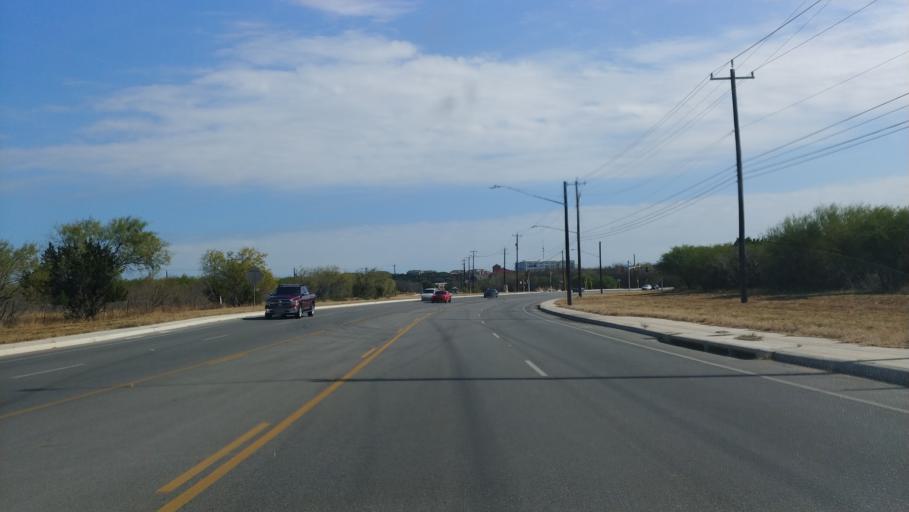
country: US
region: Texas
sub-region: Bexar County
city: Shavano Park
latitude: 29.5789
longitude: -98.6059
